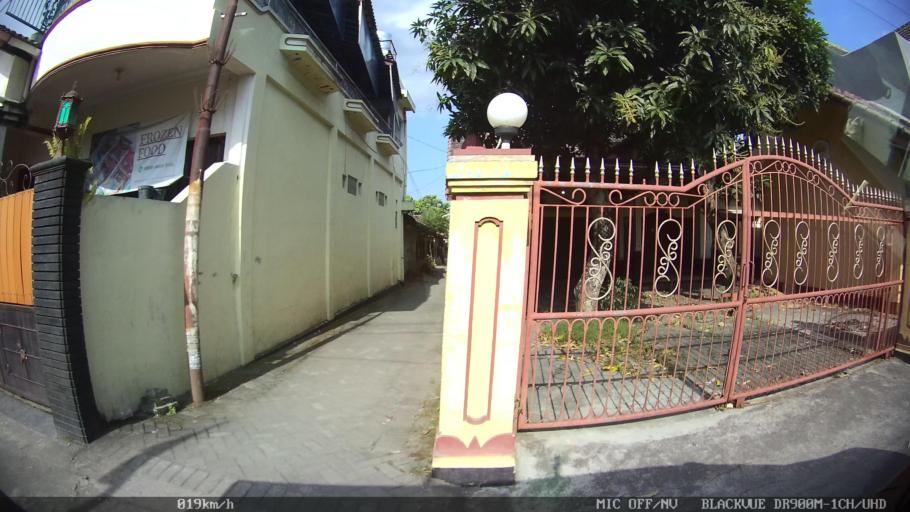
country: ID
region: Daerah Istimewa Yogyakarta
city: Gamping Lor
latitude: -7.7951
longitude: 110.3437
